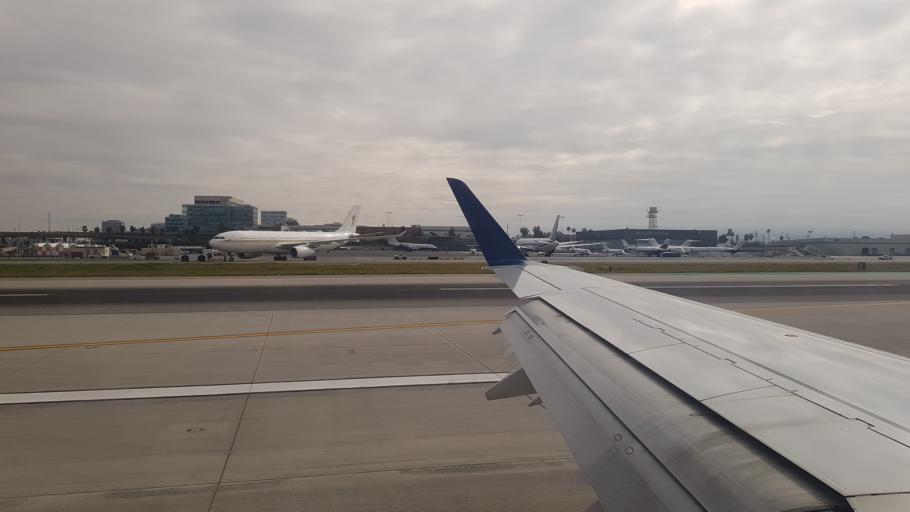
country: US
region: California
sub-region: Los Angeles County
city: El Segundo
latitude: 33.9360
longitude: -118.3983
